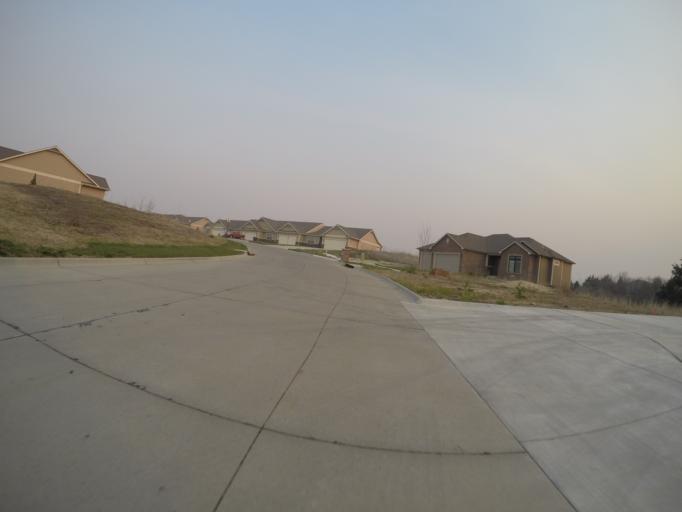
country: US
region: Kansas
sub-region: Riley County
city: Manhattan
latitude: 39.2098
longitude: -96.6509
